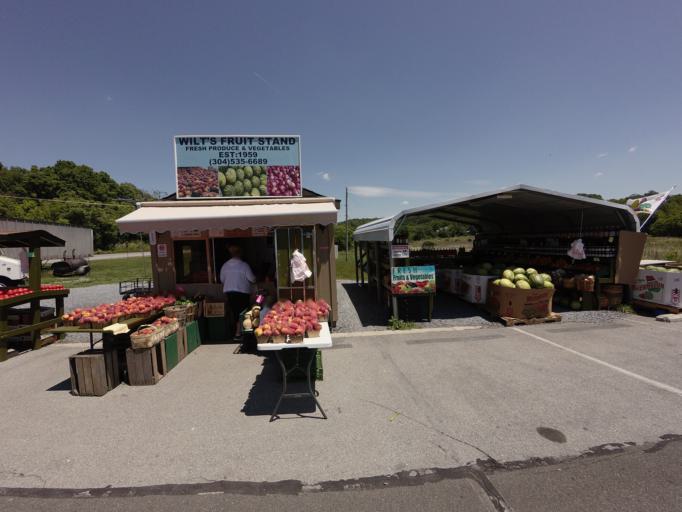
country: US
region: West Virginia
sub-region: Jefferson County
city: Bolivar
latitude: 39.3178
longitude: -77.7740
